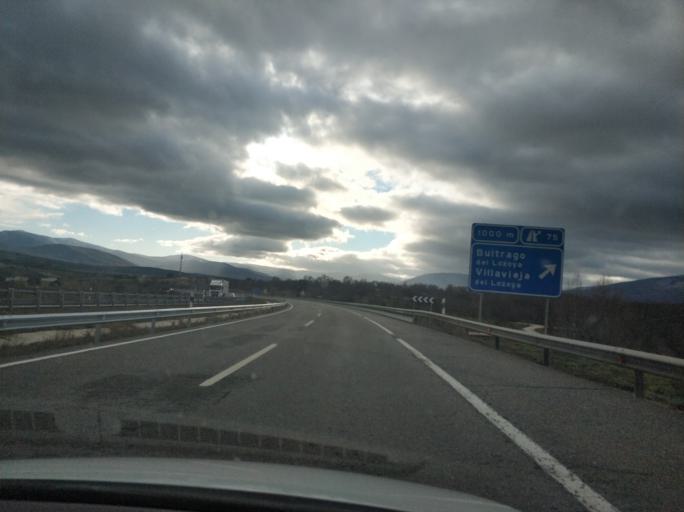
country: ES
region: Madrid
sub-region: Provincia de Madrid
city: Gascones
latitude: 41.0102
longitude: -3.6348
